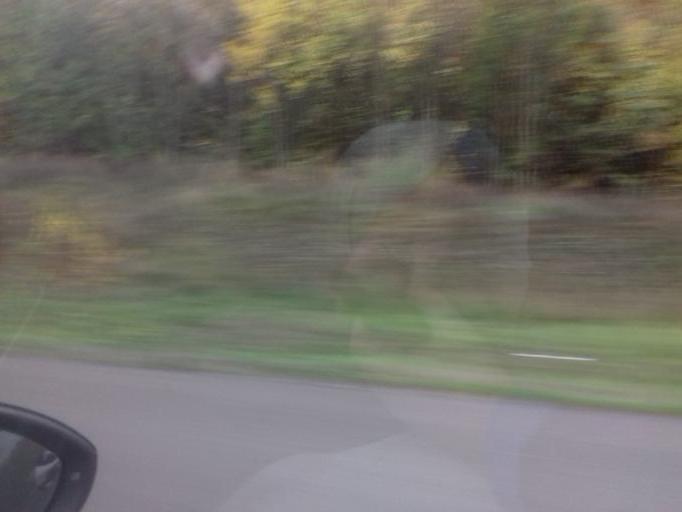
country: LU
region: Grevenmacher
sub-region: Canton de Grevenmacher
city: Flaxweiler
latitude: 49.6425
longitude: 6.3091
